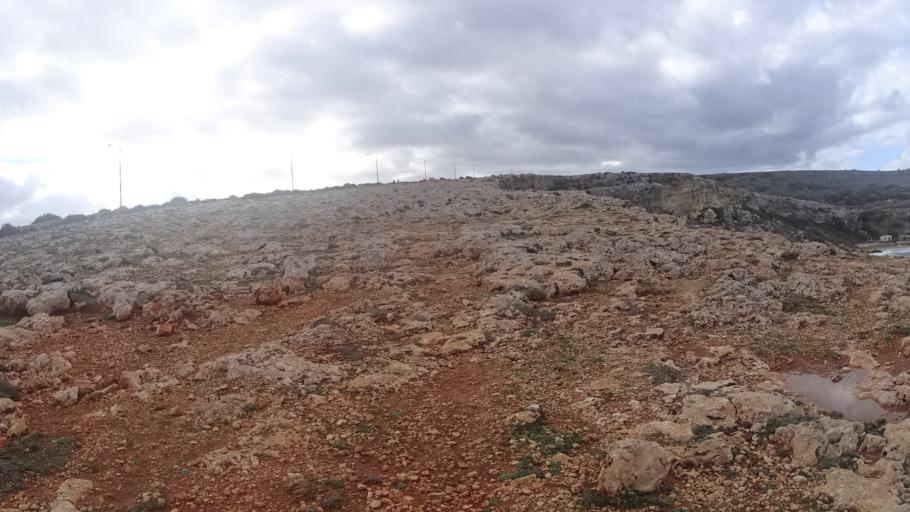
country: MT
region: Il-Mellieha
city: Mellieha
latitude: 35.9847
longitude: 14.3343
